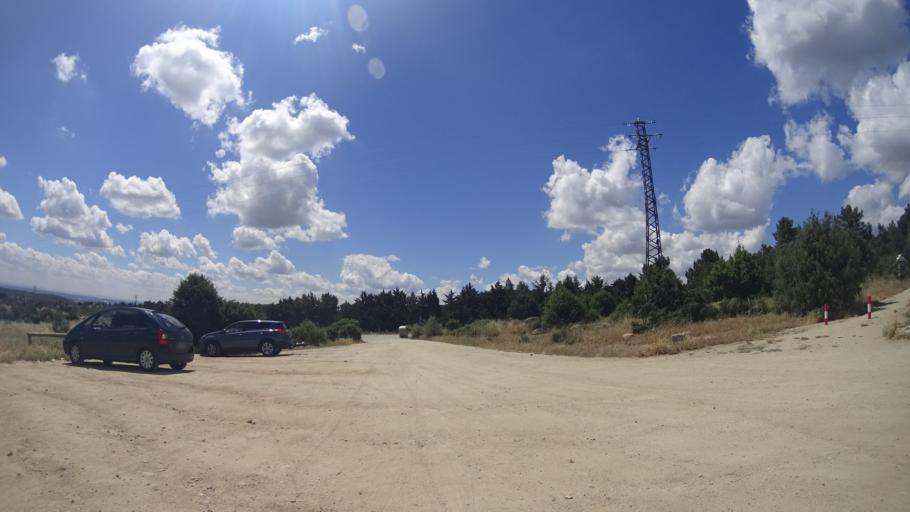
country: ES
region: Madrid
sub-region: Provincia de Madrid
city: Hoyo de Manzanares
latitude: 40.6017
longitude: -3.9154
